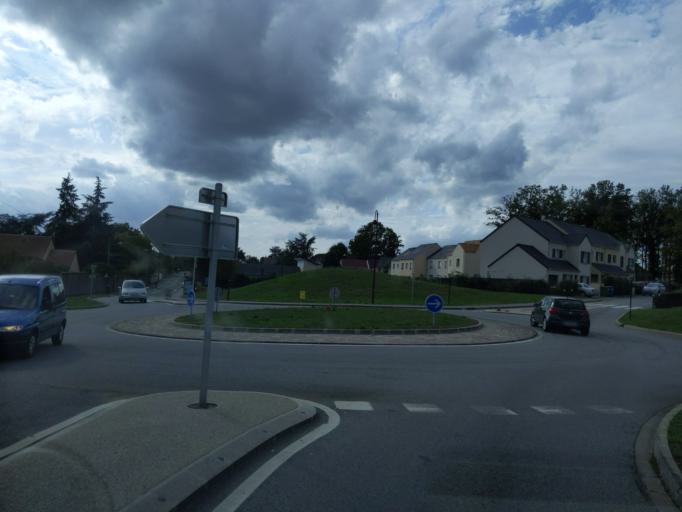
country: FR
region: Ile-de-France
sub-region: Departement des Yvelines
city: Rambouillet
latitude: 48.6492
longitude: 1.8676
